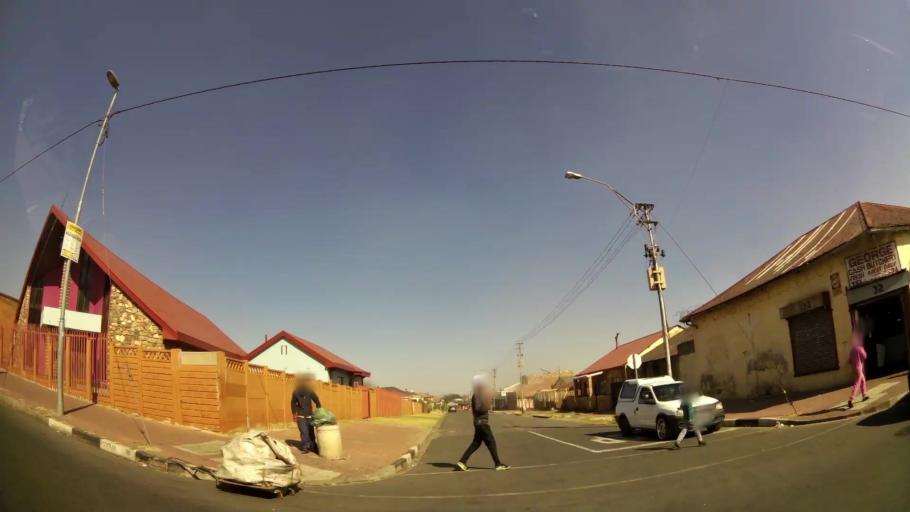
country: ZA
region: Gauteng
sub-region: City of Johannesburg Metropolitan Municipality
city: Johannesburg
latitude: -26.1860
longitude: 27.9716
